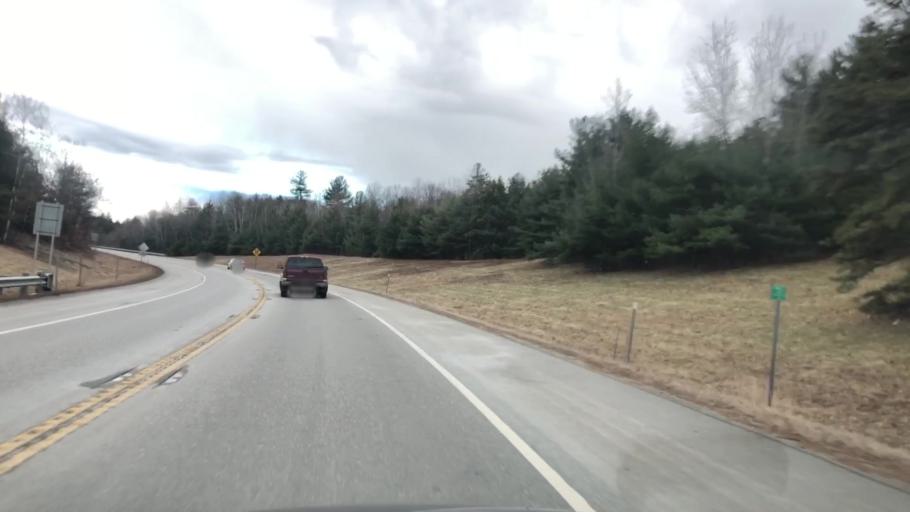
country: US
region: New Hampshire
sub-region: Hillsborough County
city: Wilton
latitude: 42.8363
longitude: -71.7003
